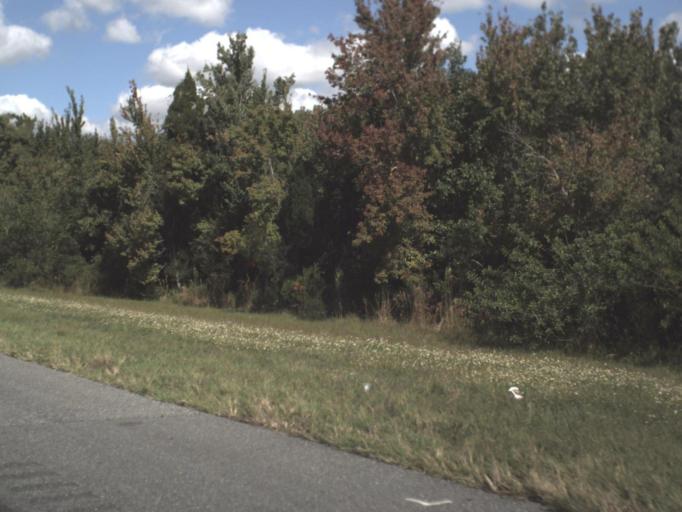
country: US
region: Florida
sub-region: Osceola County
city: Buenaventura Lakes
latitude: 28.2979
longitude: -81.3564
